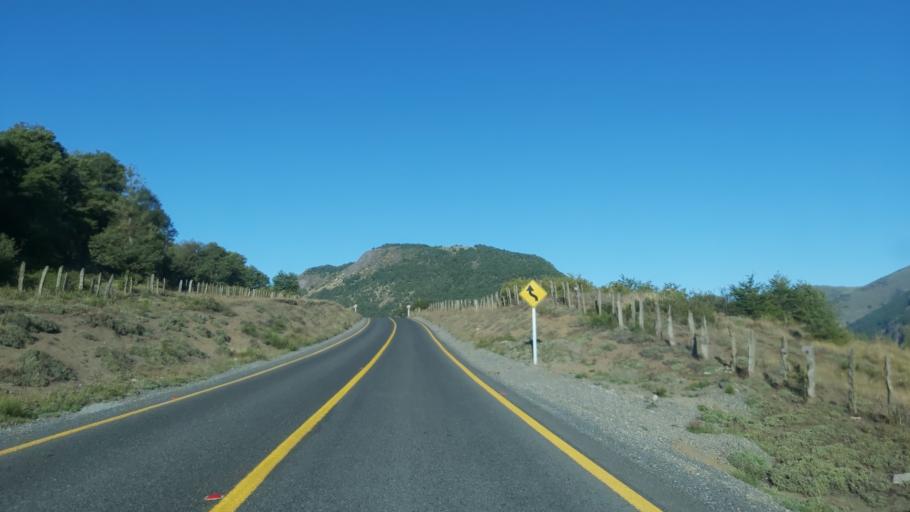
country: AR
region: Neuquen
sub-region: Departamento de Loncopue
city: Loncopue
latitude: -38.4448
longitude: -71.3484
